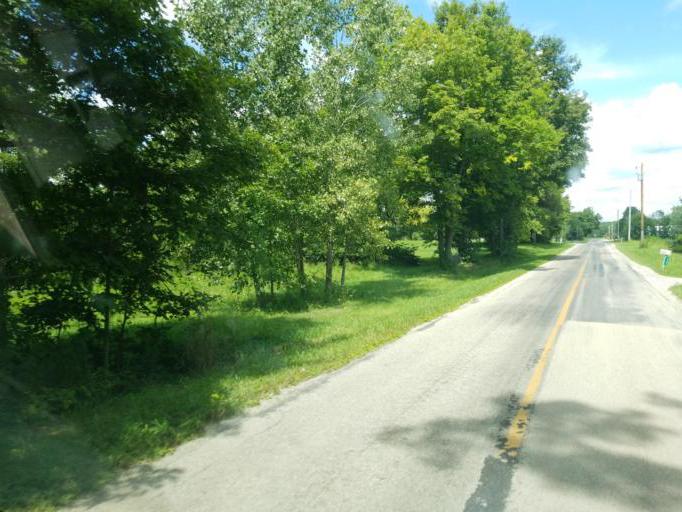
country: US
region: Ohio
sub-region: Delaware County
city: Sunbury
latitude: 40.3344
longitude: -82.8228
